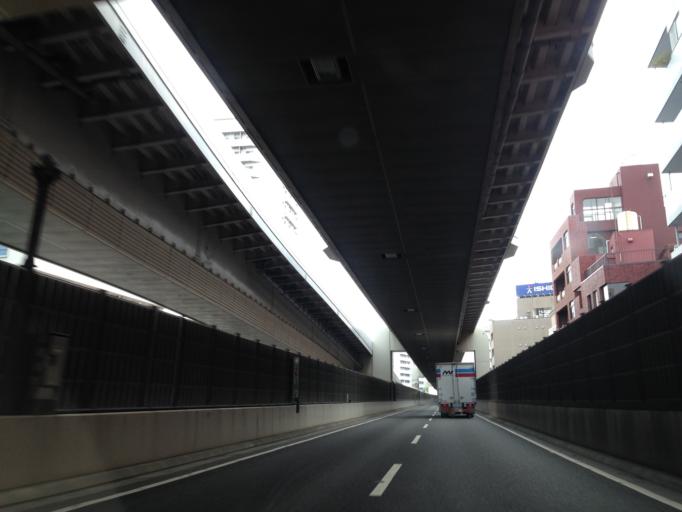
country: JP
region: Saitama
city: Kawaguchi
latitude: 35.7488
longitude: 139.7186
